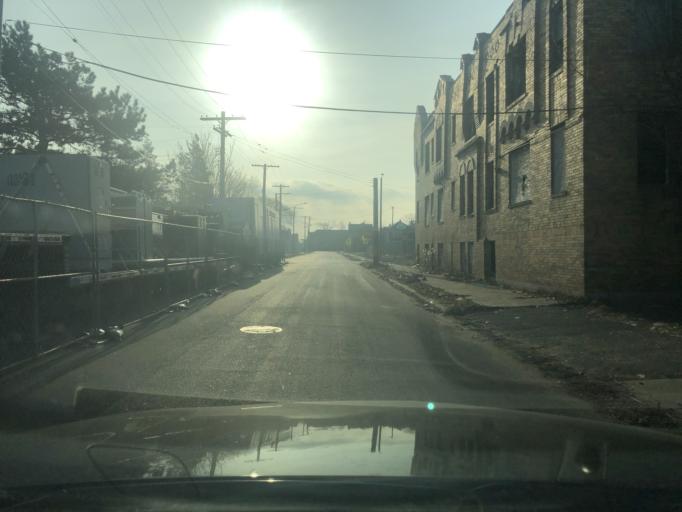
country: US
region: Michigan
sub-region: Wayne County
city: Highland Park
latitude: 42.3911
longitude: -83.1243
